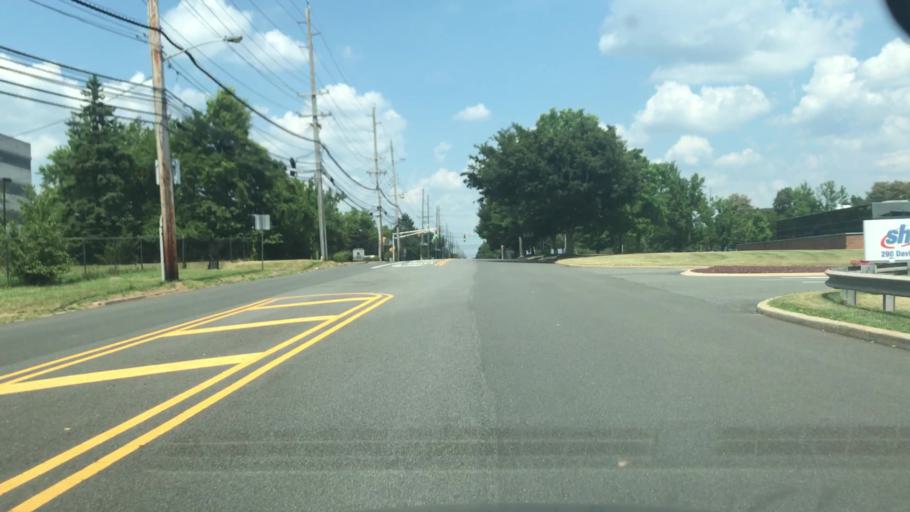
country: US
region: New Jersey
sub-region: Somerset County
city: South Bound Brook
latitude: 40.5323
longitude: -74.5288
